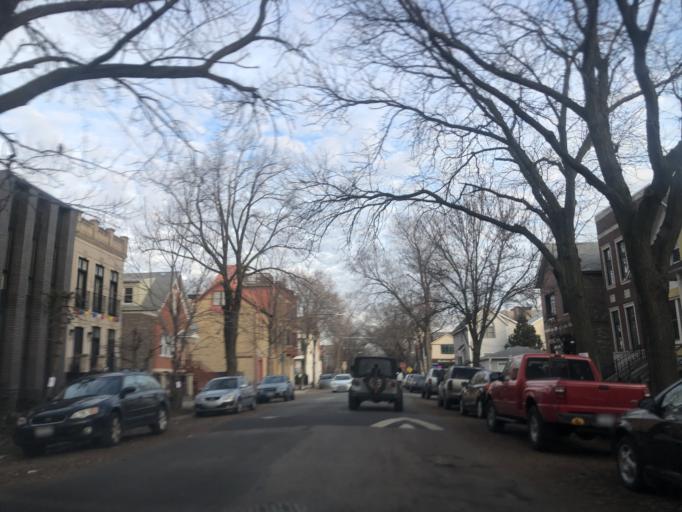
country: US
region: Illinois
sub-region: Cook County
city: Chicago
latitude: 41.9114
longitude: -87.6726
